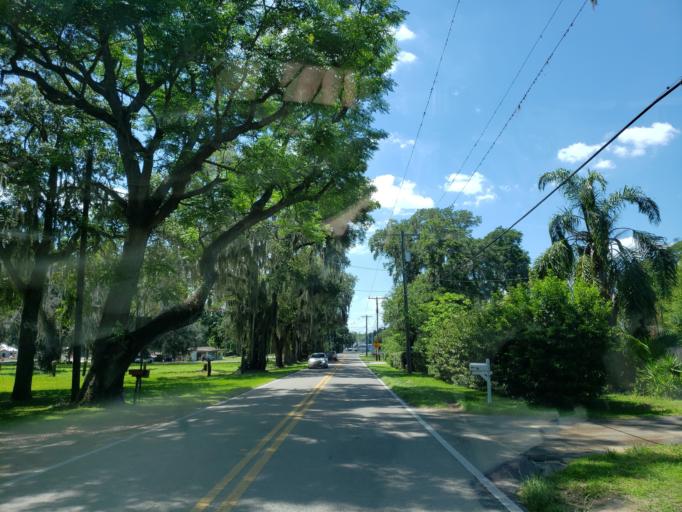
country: US
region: Florida
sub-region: Hillsborough County
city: Brandon
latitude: 27.9219
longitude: -82.2668
